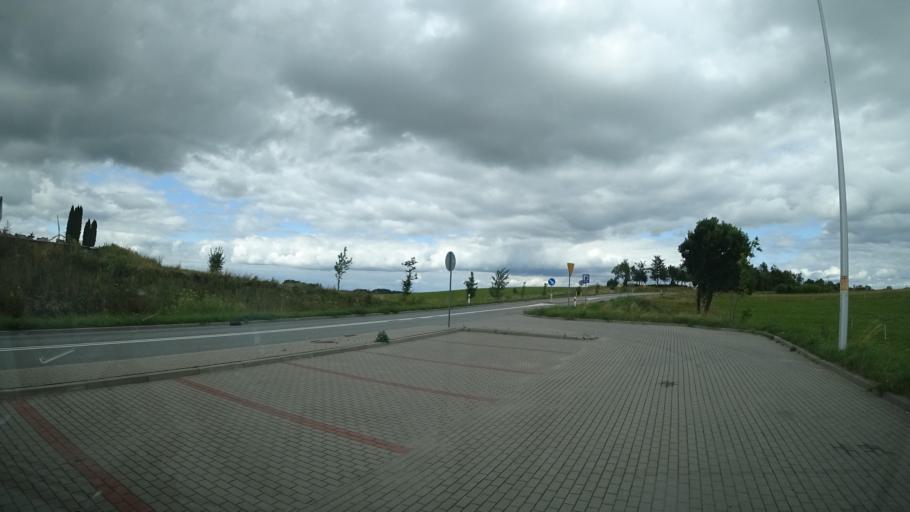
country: PL
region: Warmian-Masurian Voivodeship
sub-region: Powiat goldapski
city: Goldap
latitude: 54.2287
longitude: 22.2450
